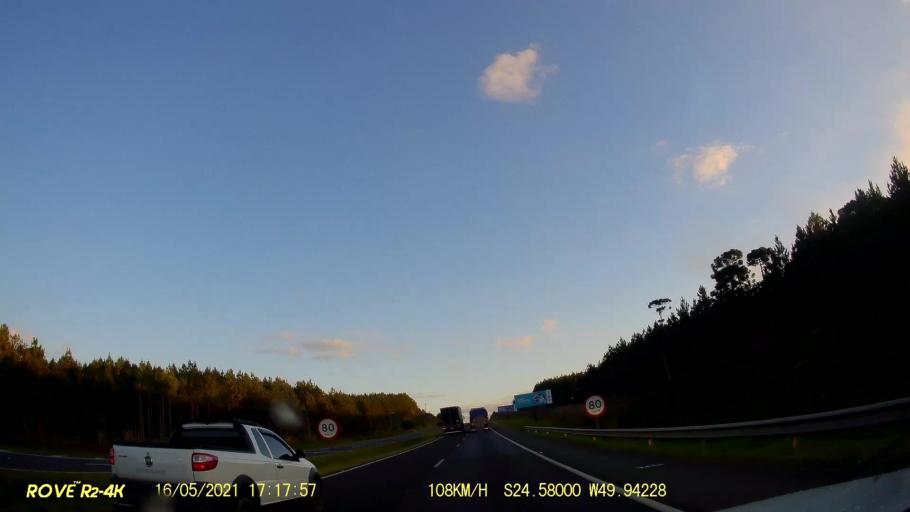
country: BR
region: Parana
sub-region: Pirai Do Sul
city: Pirai do Sul
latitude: -24.5804
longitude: -49.9425
